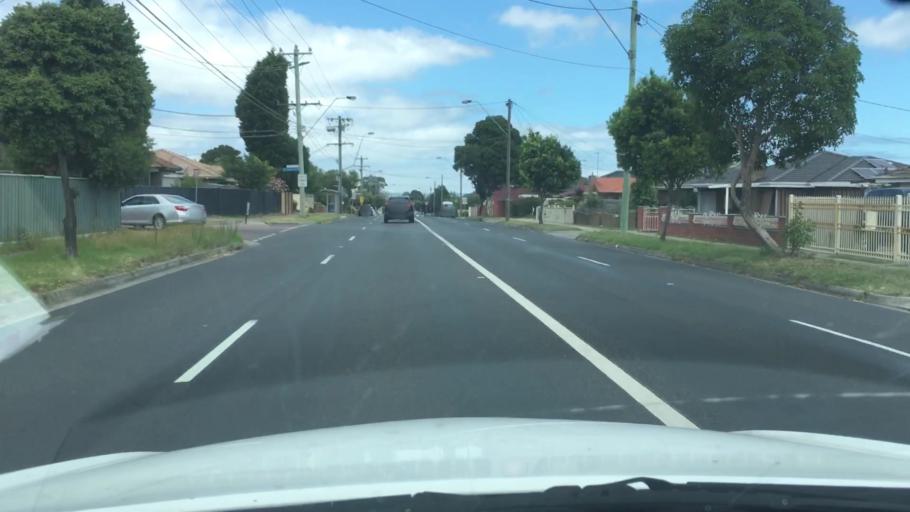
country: AU
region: Victoria
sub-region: Greater Dandenong
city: Keysborough
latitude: -37.9818
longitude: 145.1844
